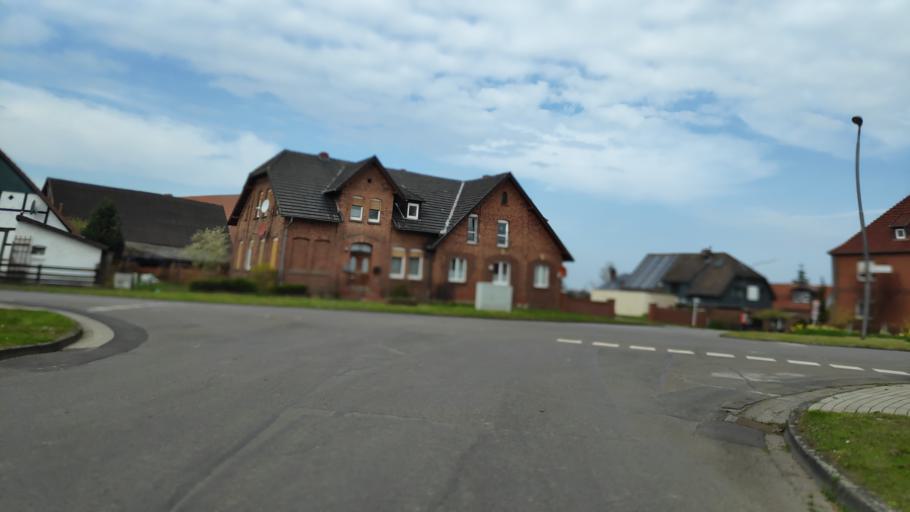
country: DE
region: North Rhine-Westphalia
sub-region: Regierungsbezirk Detmold
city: Minden
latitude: 52.2690
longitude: 8.9504
